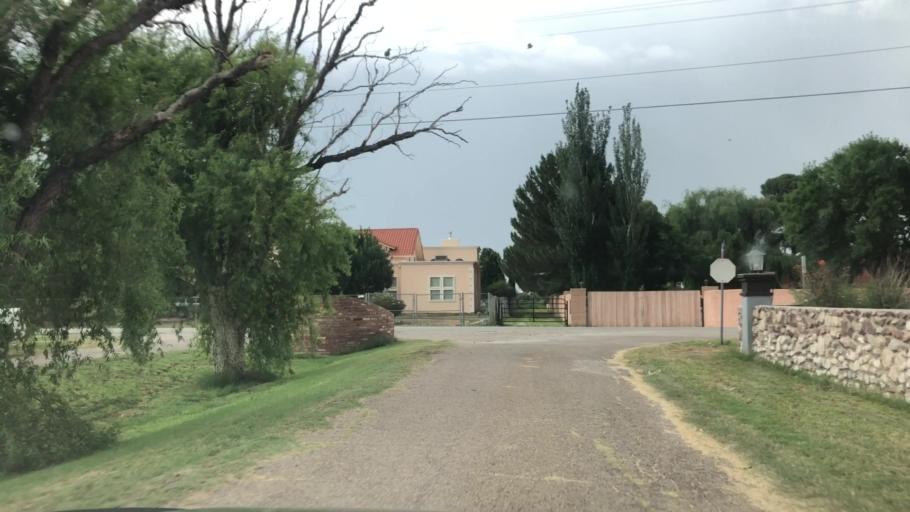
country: US
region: Texas
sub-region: El Paso County
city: Canutillo
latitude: 31.9017
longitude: -106.6396
